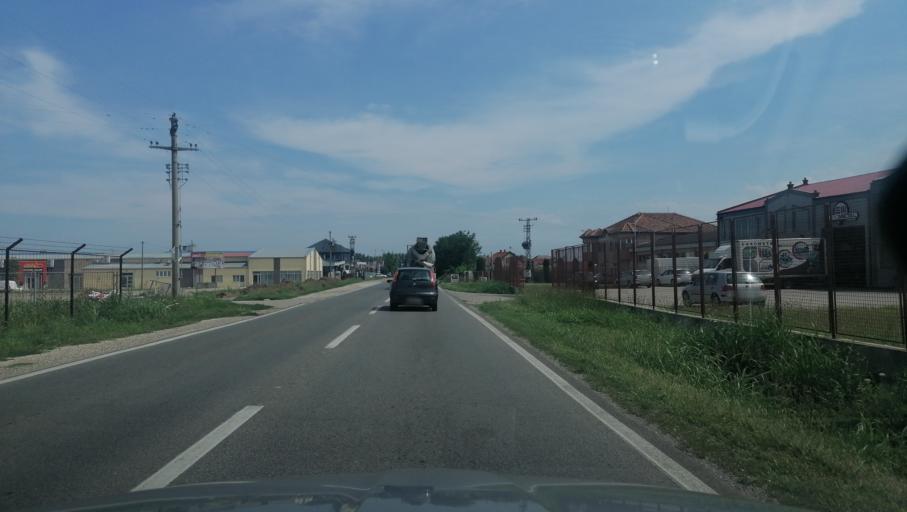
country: BA
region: Republika Srpska
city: Velika Obarska
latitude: 44.7683
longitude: 19.1626
